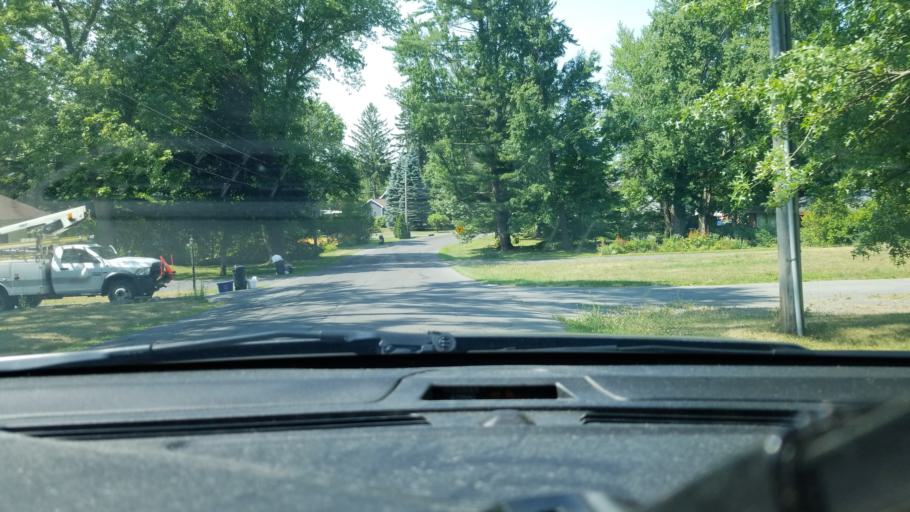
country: US
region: New York
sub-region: Onondaga County
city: Liverpool
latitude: 43.1137
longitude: -76.2202
